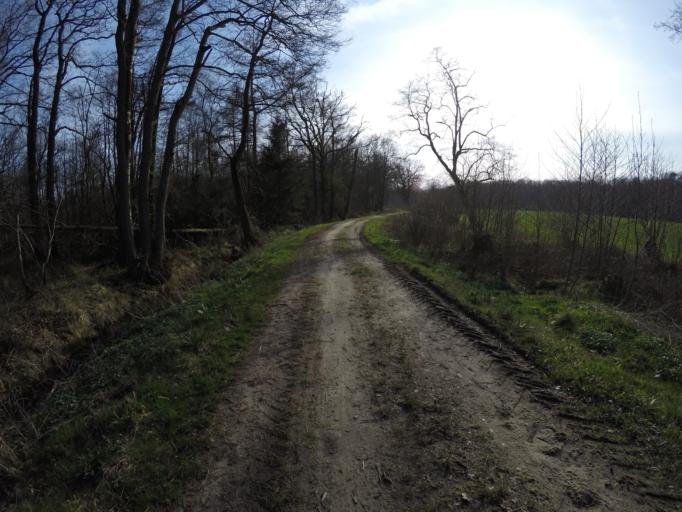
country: DE
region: Schleswig-Holstein
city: Hemdingen
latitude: 53.7470
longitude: 9.8407
